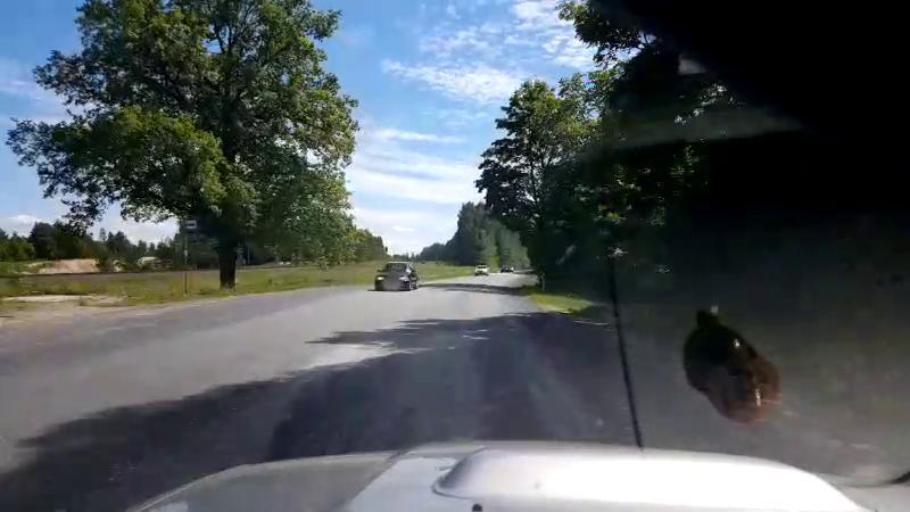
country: EE
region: Laeaene-Virumaa
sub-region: Rakke vald
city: Rakke
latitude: 58.8798
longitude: 26.2949
